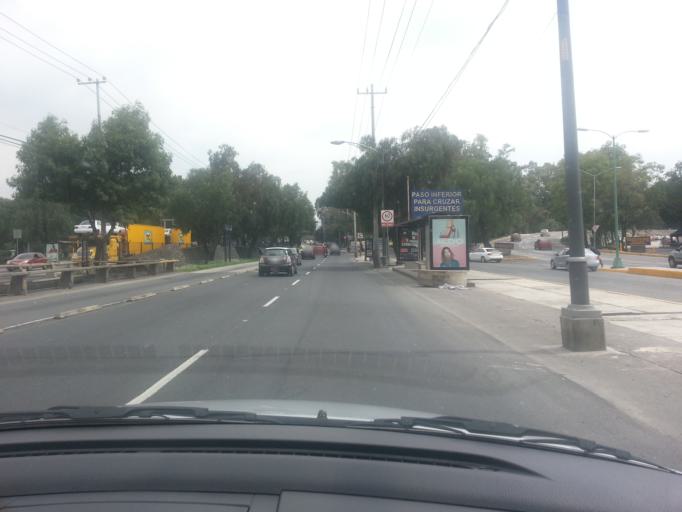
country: MX
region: Mexico City
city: Magdalena Contreras
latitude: 19.3317
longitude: -99.1897
